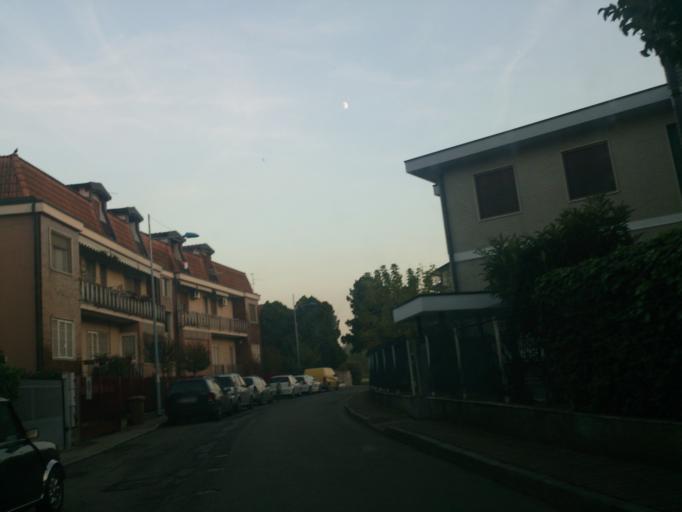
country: IT
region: Lombardy
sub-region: Citta metropolitana di Milano
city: San Donato Milanese
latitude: 45.4090
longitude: 9.2766
